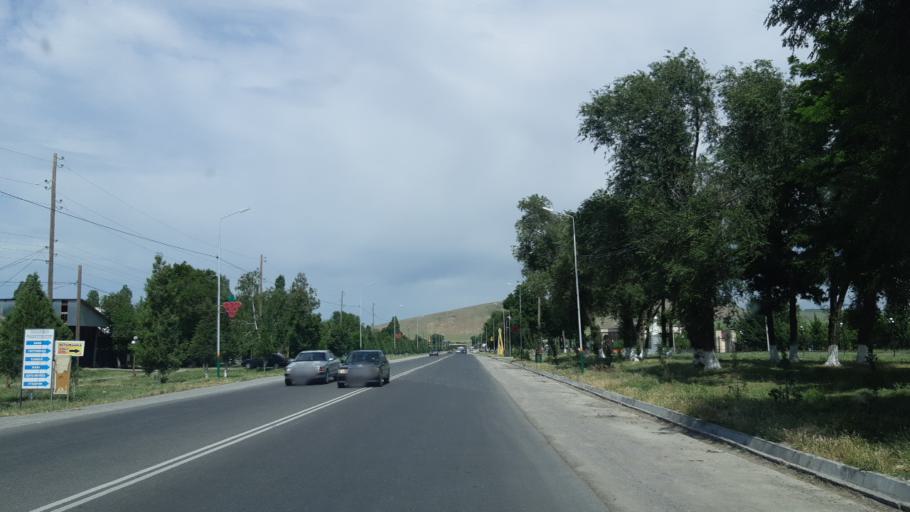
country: KZ
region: Ongtustik Qazaqstan
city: Turar Ryskulov
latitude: 42.5449
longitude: 70.3303
